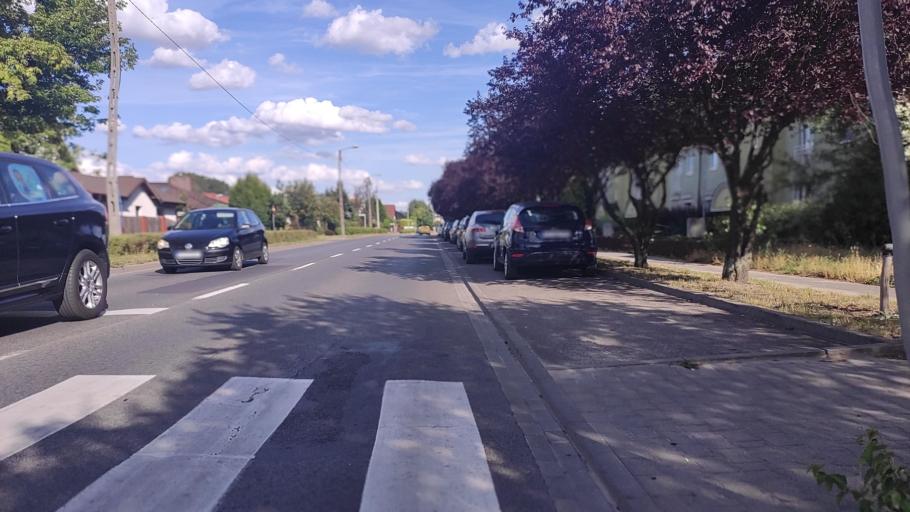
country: PL
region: Greater Poland Voivodeship
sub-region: Powiat poznanski
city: Swarzedz
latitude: 52.3983
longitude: 17.0684
